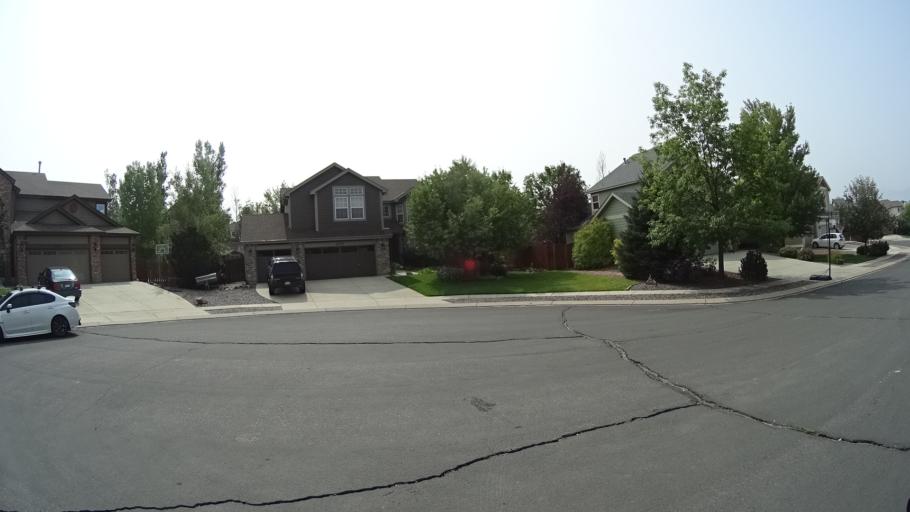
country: US
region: Colorado
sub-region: El Paso County
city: Cimarron Hills
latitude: 38.9277
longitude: -104.7471
